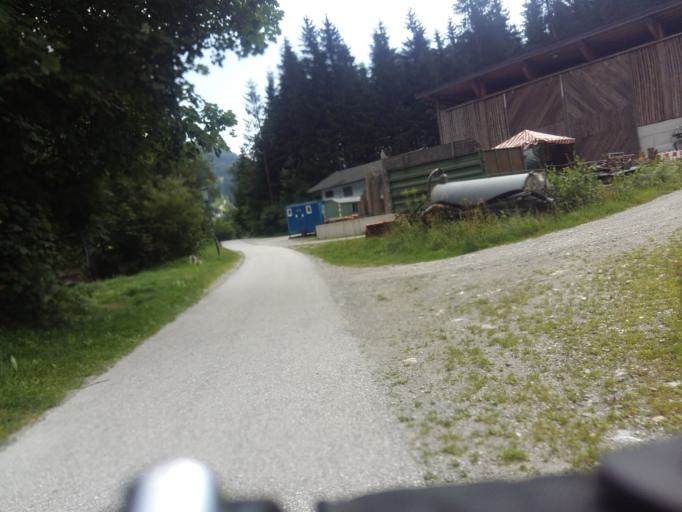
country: AT
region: Salzburg
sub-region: Politischer Bezirk Sankt Johann im Pongau
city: Schwarzach im Pongau
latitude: 47.2499
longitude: 13.1987
